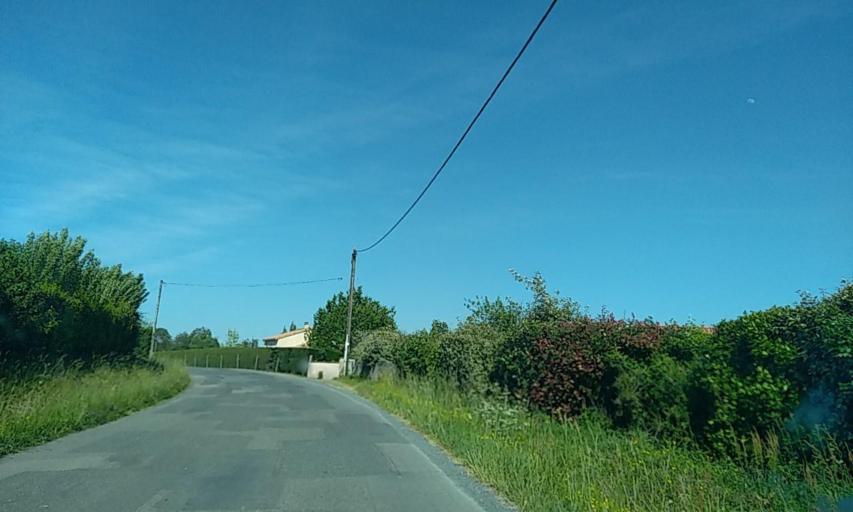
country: FR
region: Poitou-Charentes
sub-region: Departement des Deux-Sevres
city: Boisme
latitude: 46.7750
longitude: -0.4297
